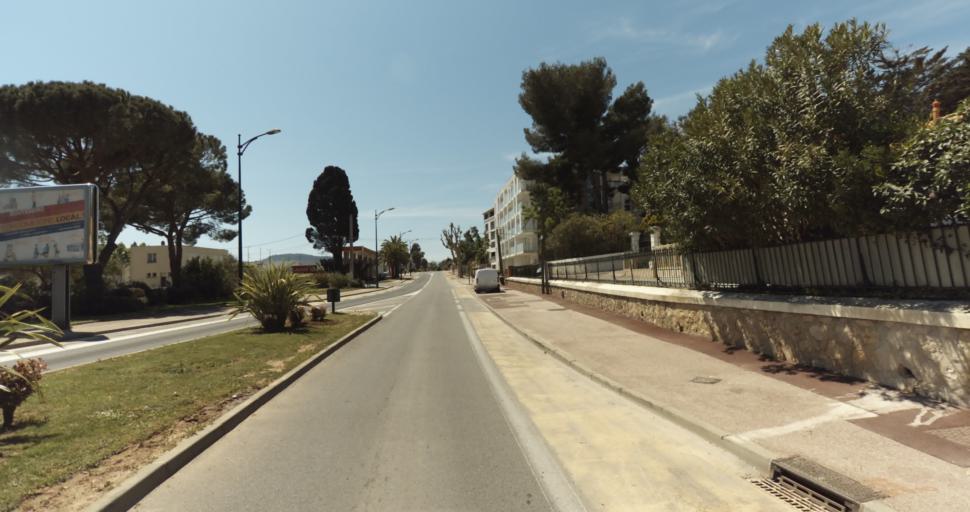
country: FR
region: Provence-Alpes-Cote d'Azur
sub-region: Departement du Var
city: Hyeres
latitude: 43.1247
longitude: 6.1499
